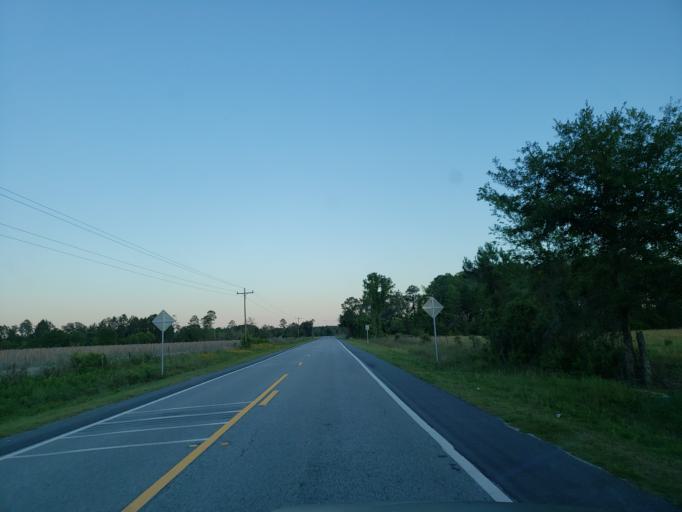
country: US
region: Georgia
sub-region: Echols County
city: Statenville
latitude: 30.5682
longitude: -83.1583
